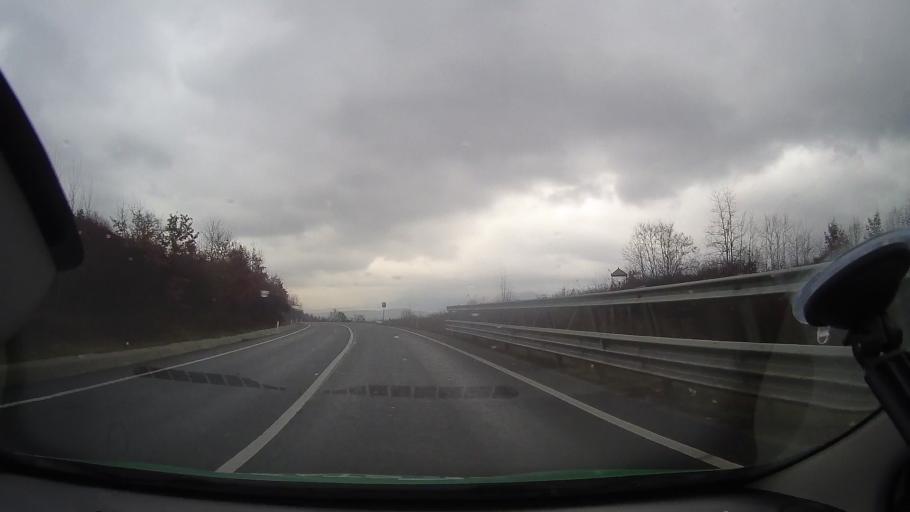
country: RO
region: Hunedoara
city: Vata de Jos
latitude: 46.2075
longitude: 22.5809
